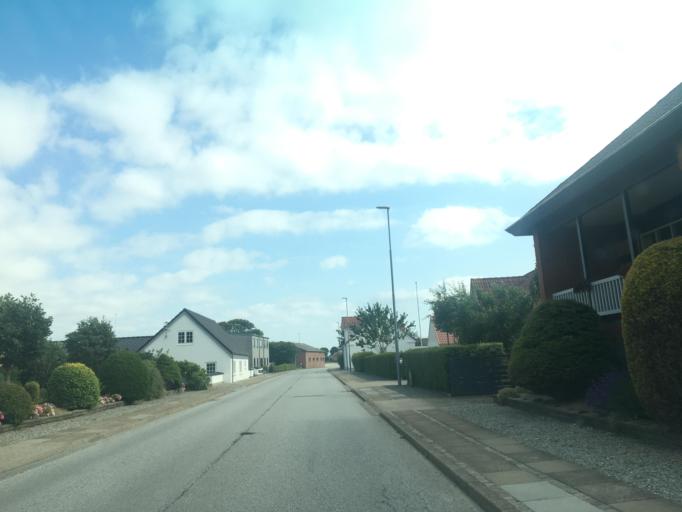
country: DK
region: North Denmark
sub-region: Thisted Kommune
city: Thisted
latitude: 56.8802
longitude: 8.6280
